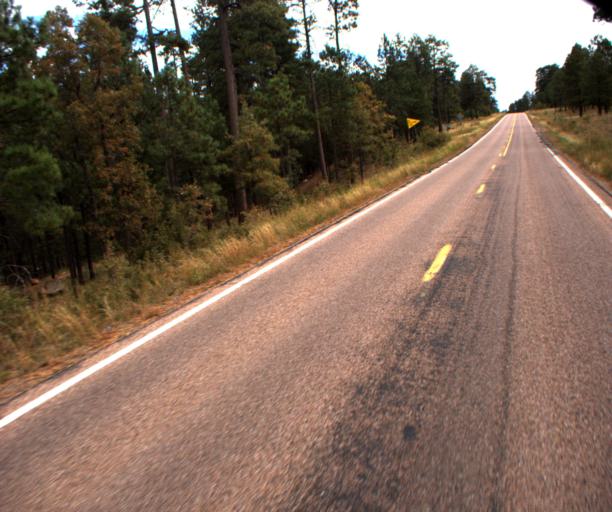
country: US
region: Arizona
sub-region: Navajo County
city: Heber-Overgaard
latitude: 34.3368
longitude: -110.7379
